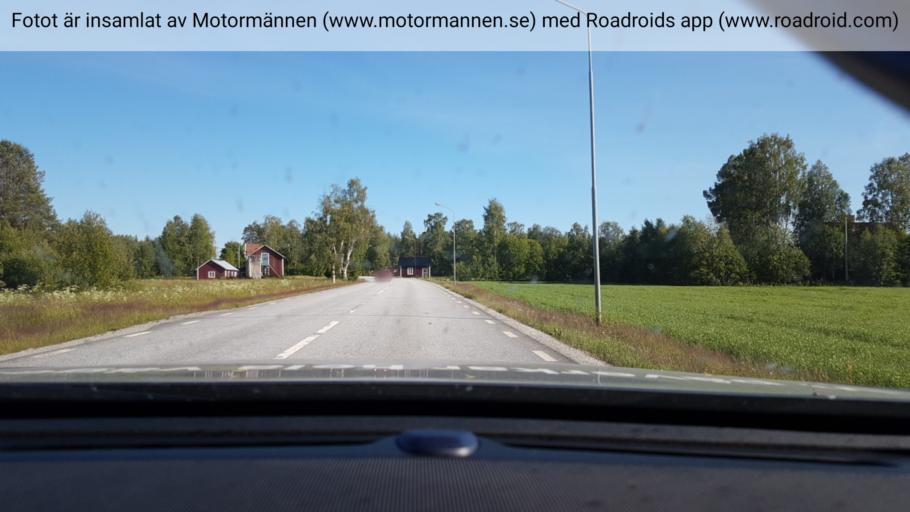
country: SE
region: Vaesterbotten
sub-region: Vindelns Kommun
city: Vindeln
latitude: 64.1215
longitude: 19.5613
